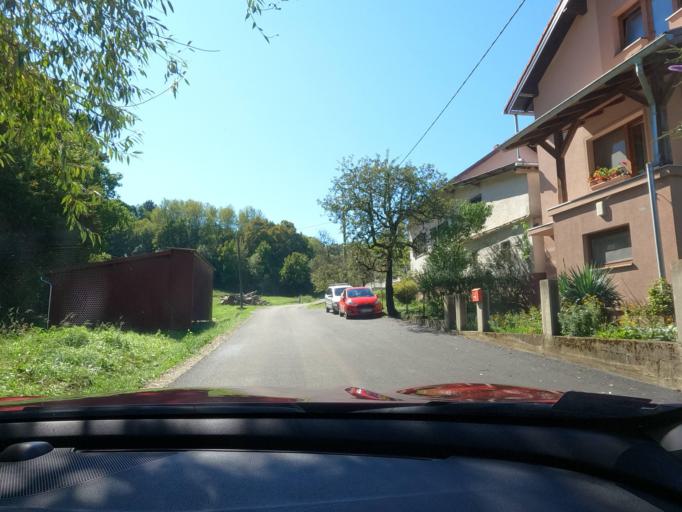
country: HR
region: Sisacko-Moslavacka
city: Petrinja
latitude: 45.4284
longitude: 16.2675
